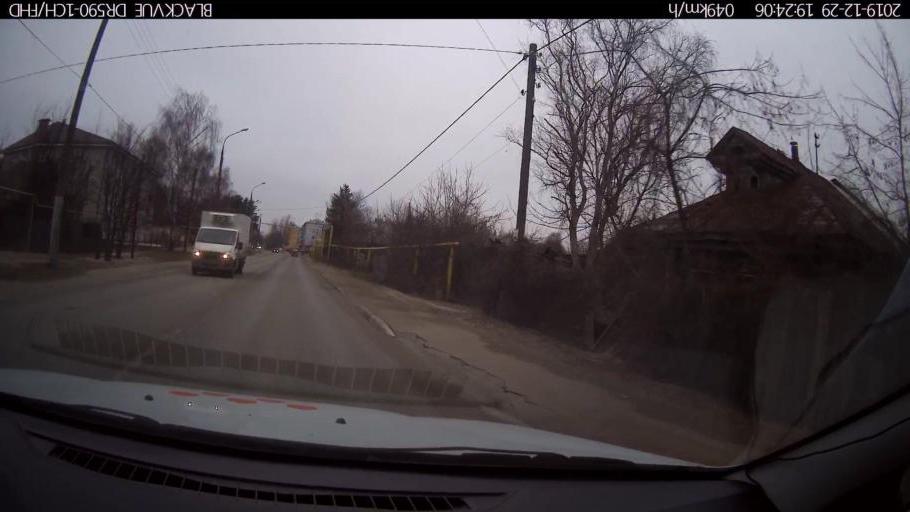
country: RU
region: Nizjnij Novgorod
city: Nizhniy Novgorod
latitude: 56.3355
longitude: 43.8676
